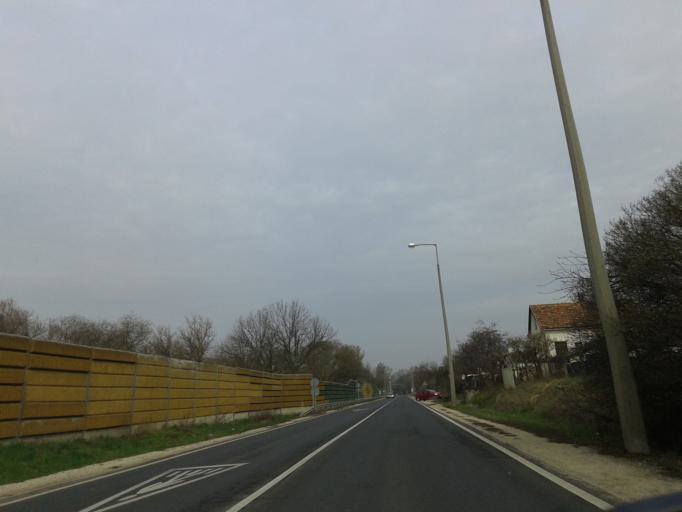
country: HU
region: Komarom-Esztergom
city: Tatabanya
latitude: 47.5881
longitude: 18.4005
